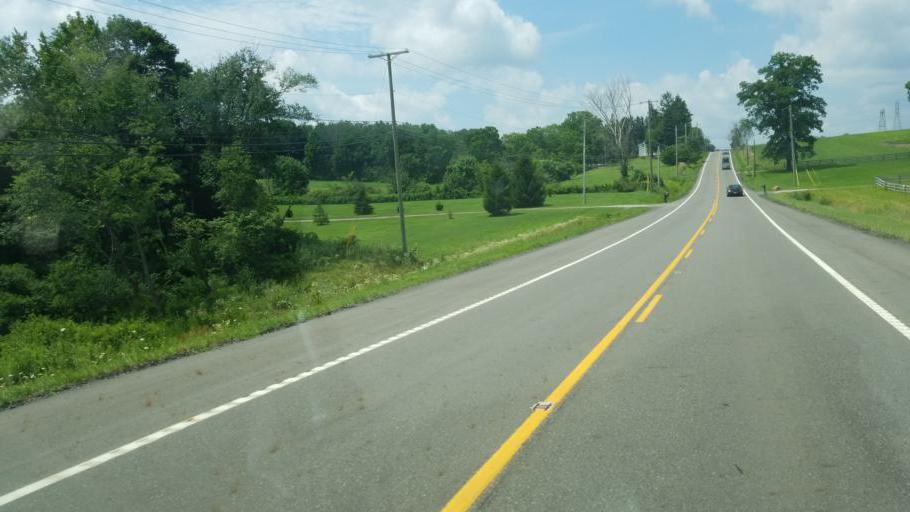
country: US
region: Ohio
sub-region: Columbiana County
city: Lisbon
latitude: 40.7700
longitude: -80.7950
